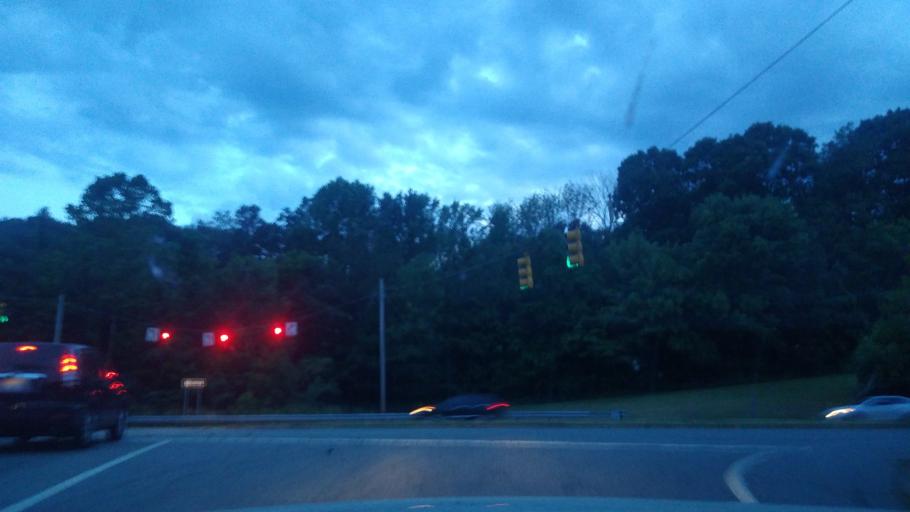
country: US
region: North Carolina
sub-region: Guilford County
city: Greensboro
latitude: 36.0988
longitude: -79.8330
